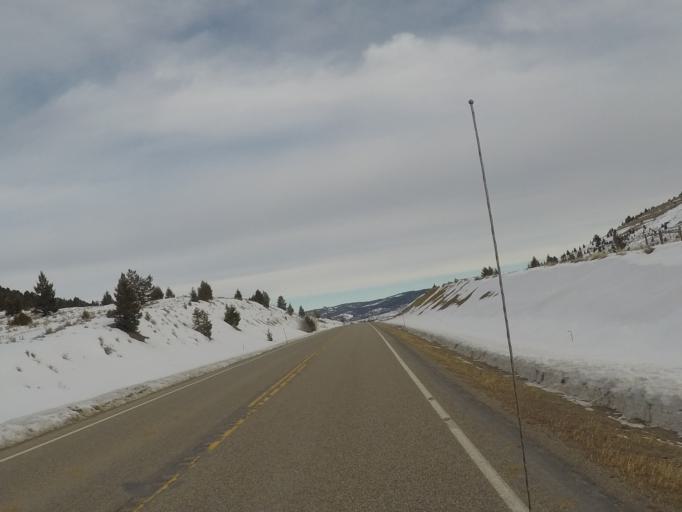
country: US
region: Montana
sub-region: Meagher County
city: White Sulphur Springs
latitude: 46.6441
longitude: -110.8651
